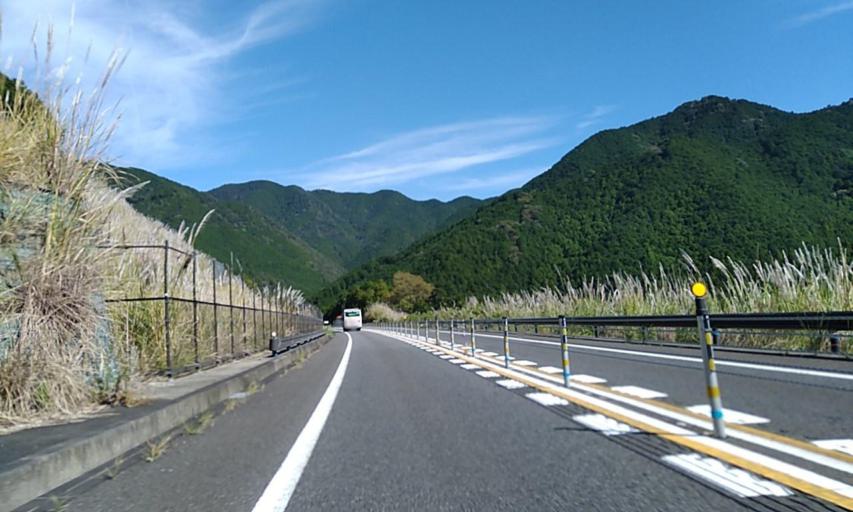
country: JP
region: Mie
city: Owase
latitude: 33.9401
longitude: 136.1500
